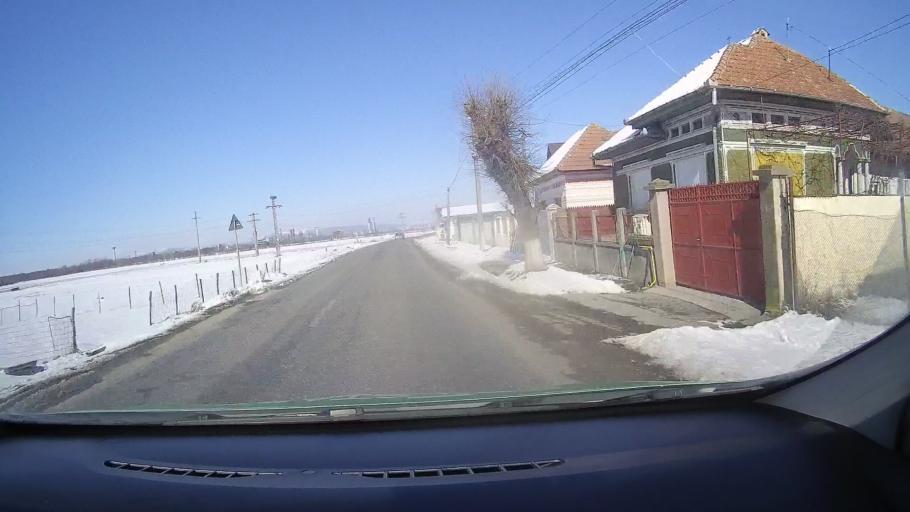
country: RO
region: Brasov
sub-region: Comuna Harseni
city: Harseni
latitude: 45.7936
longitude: 24.9955
